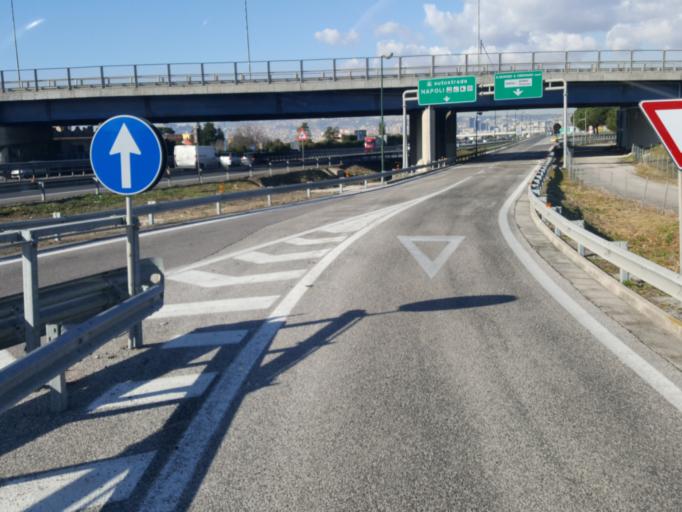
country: IT
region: Campania
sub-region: Provincia di Napoli
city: San Giorgio a Cremano
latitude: 40.8397
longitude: 14.3331
